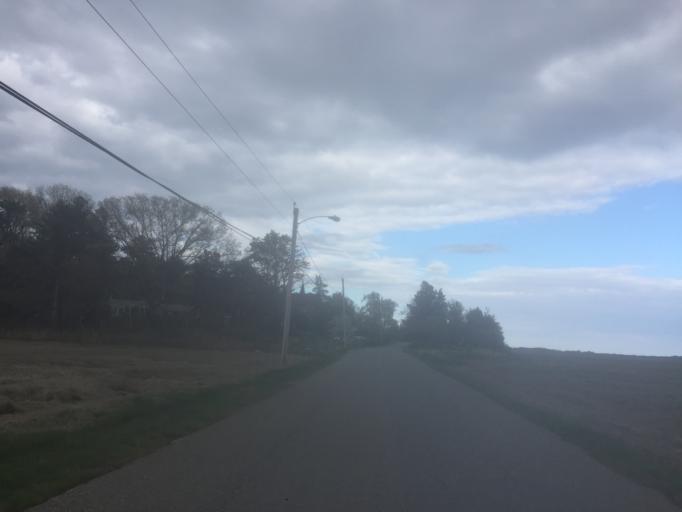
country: US
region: Massachusetts
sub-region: Essex County
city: Newburyport
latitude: 42.7795
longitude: -70.8303
